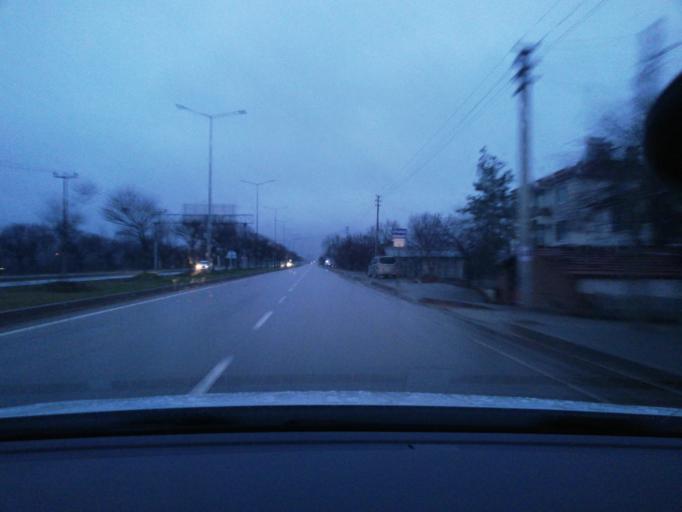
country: TR
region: Bolu
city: Bolu
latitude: 40.7017
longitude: 31.6181
